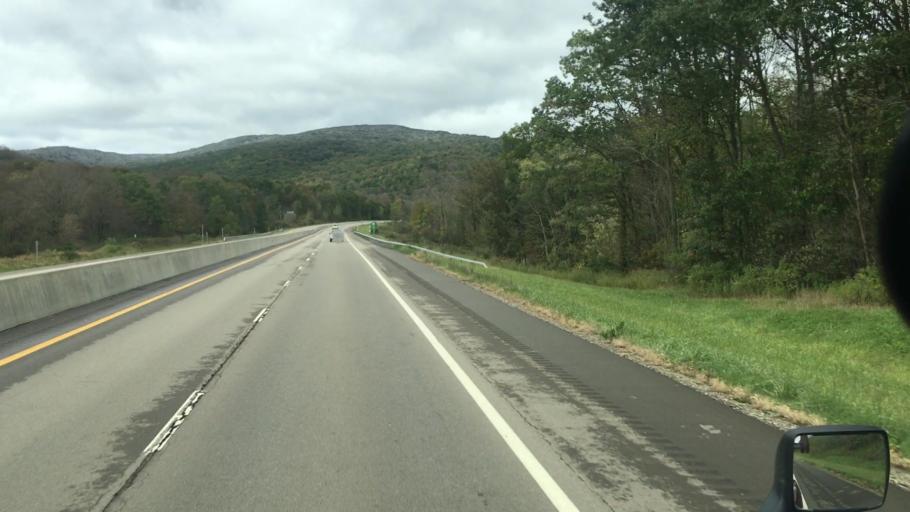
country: US
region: New York
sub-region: Cattaraugus County
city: Salamanca
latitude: 42.0966
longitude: -78.6562
